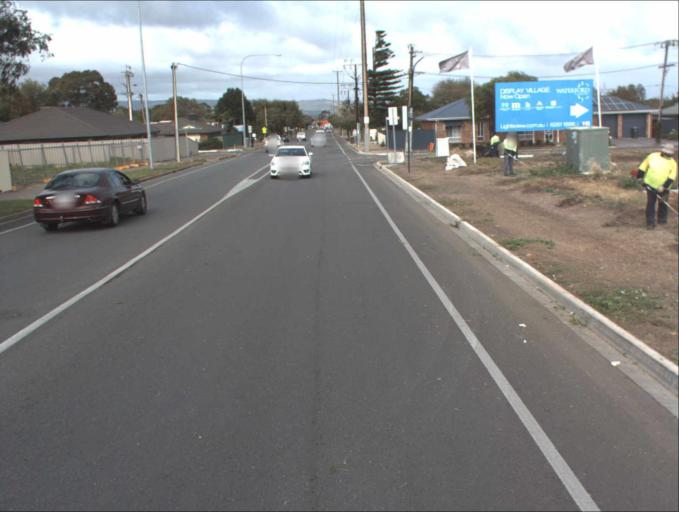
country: AU
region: South Australia
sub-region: Port Adelaide Enfield
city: Klemzig
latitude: -34.8645
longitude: 138.6366
